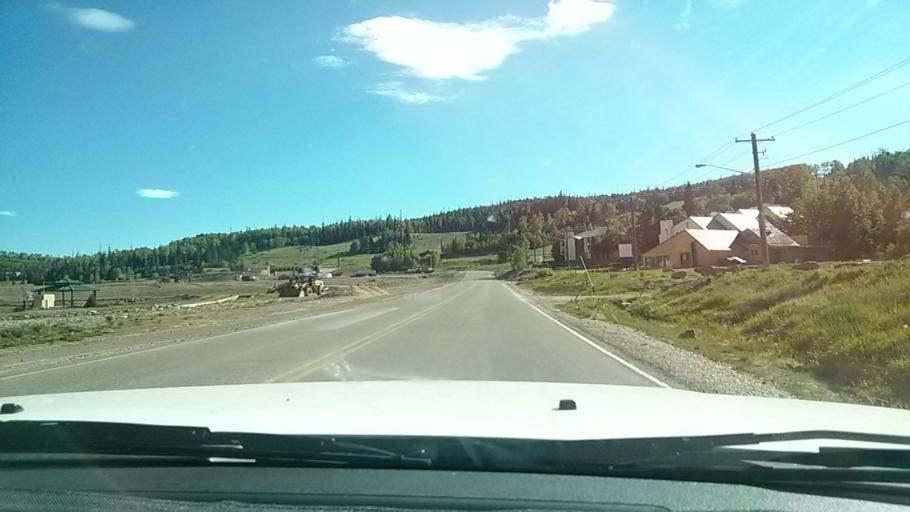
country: US
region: Utah
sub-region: Iron County
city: Parowan
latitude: 37.6922
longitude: -112.8509
